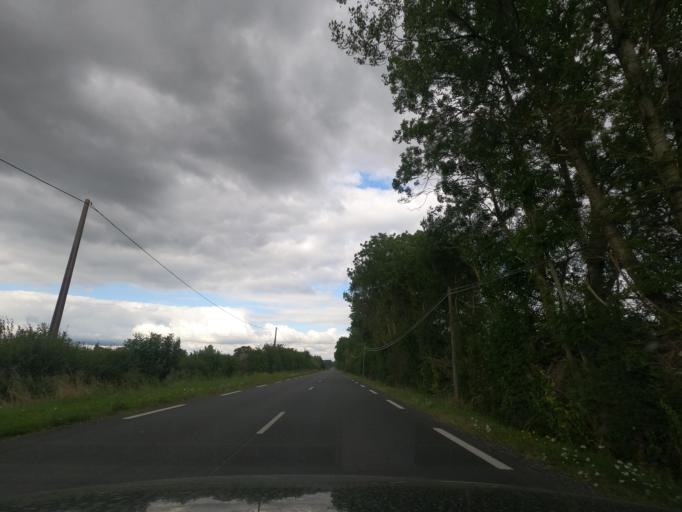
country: FR
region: Lower Normandy
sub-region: Departement de l'Orne
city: Gace
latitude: 48.8603
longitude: 0.3667
